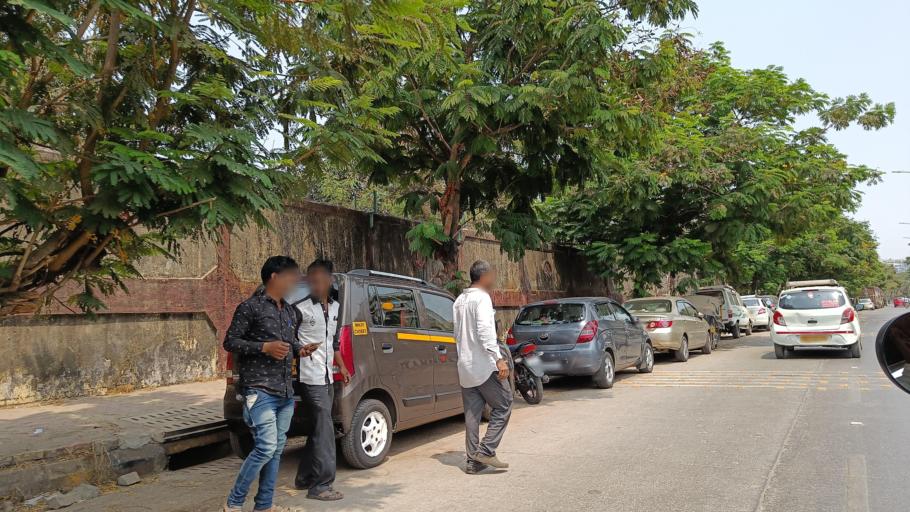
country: IN
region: Maharashtra
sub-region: Mumbai Suburban
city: Mumbai
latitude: 19.0666
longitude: 72.8558
